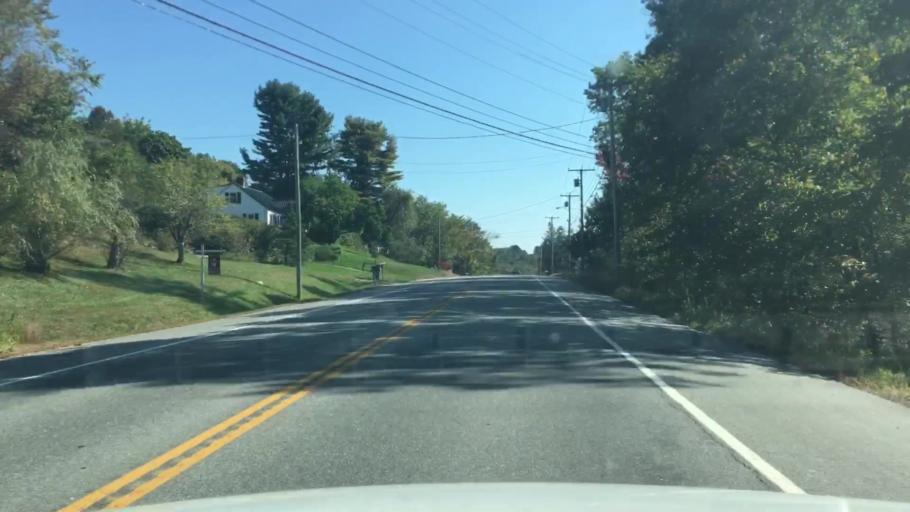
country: US
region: Maine
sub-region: Androscoggin County
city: Lisbon Falls
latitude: 43.9884
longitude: -70.0441
